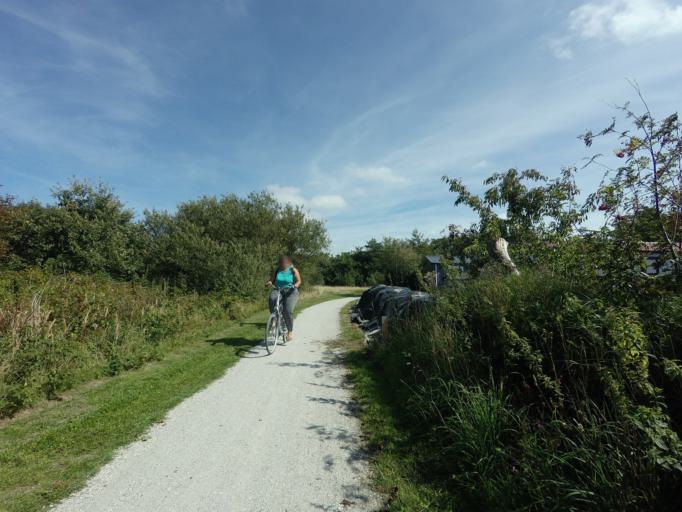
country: NL
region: Friesland
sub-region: Gemeente Ameland
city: Hollum
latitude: 53.4512
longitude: 5.6476
